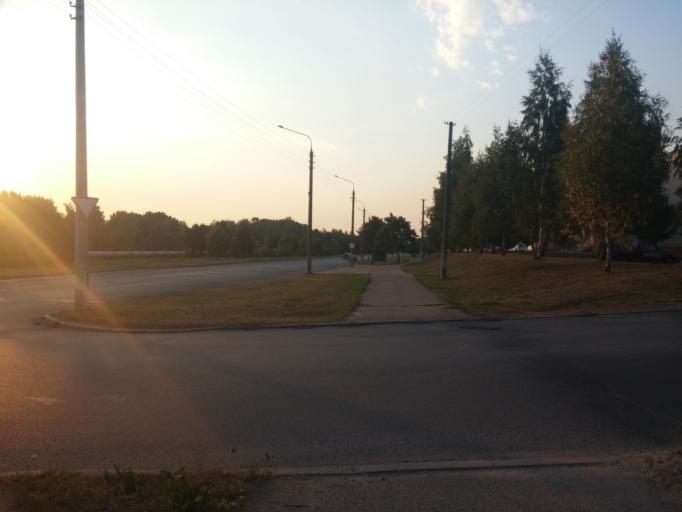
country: BY
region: Minsk
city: Vyaliki Trastsyanets
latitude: 53.8358
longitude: 27.6801
